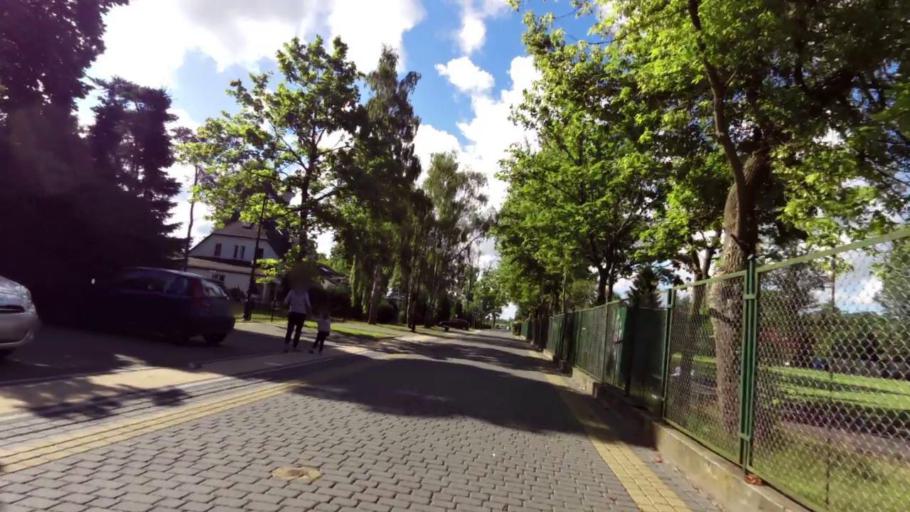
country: PL
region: West Pomeranian Voivodeship
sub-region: Powiat koszalinski
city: Mielno
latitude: 54.2629
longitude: 16.0682
